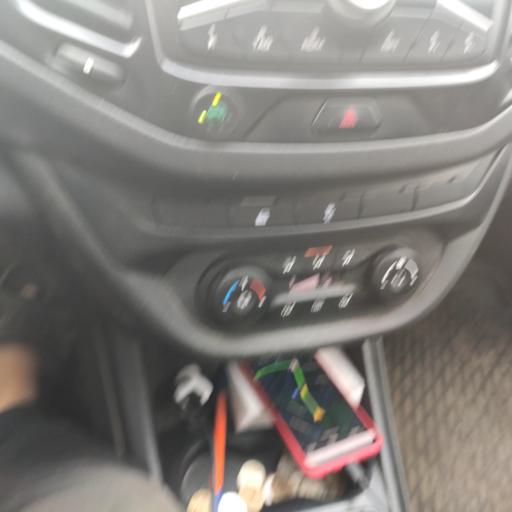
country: RU
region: Perm
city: Perm
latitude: 58.0902
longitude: 56.4036
